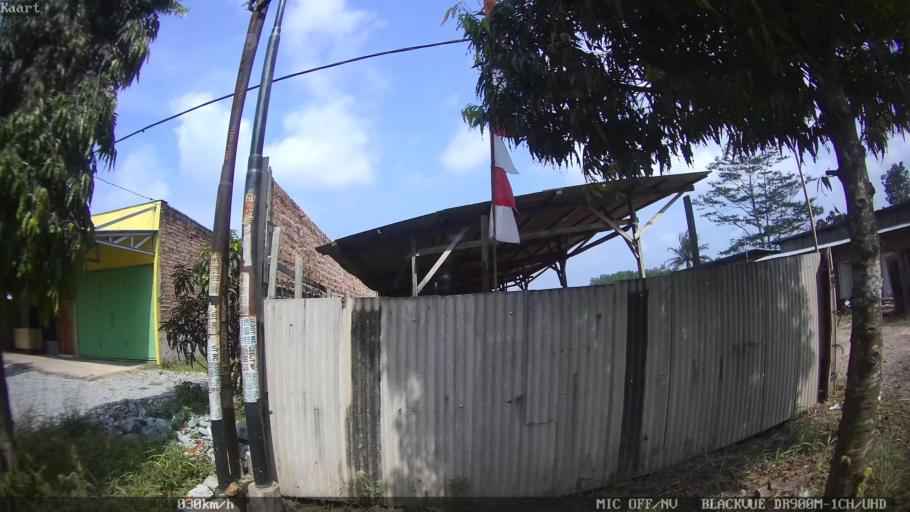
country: ID
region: Lampung
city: Kedaton
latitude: -5.3216
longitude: 105.2859
